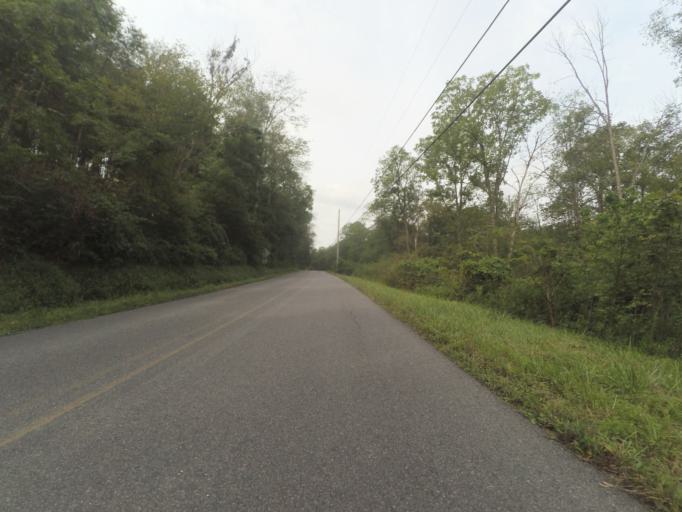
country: US
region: Pennsylvania
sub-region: Huntingdon County
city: McConnellstown
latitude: 40.5478
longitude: -78.1054
